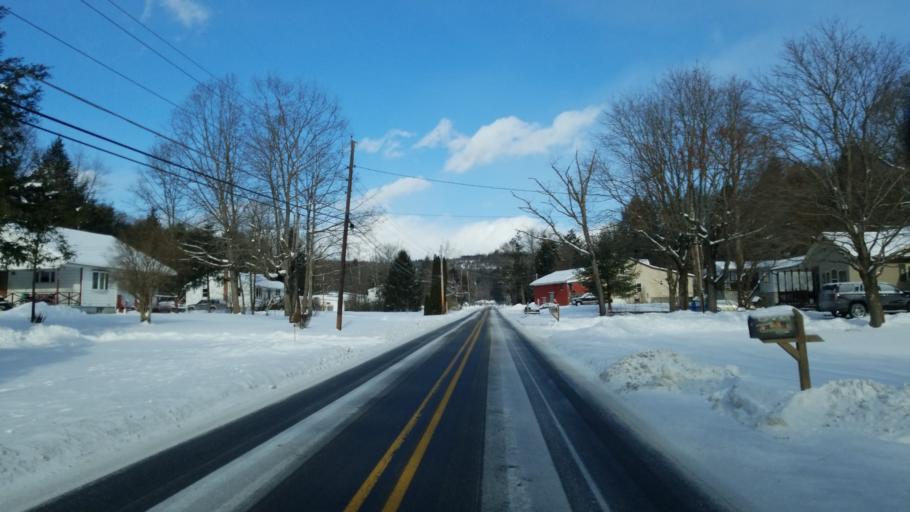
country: US
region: Pennsylvania
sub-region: Clearfield County
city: Hyde
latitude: 41.0074
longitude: -78.4686
